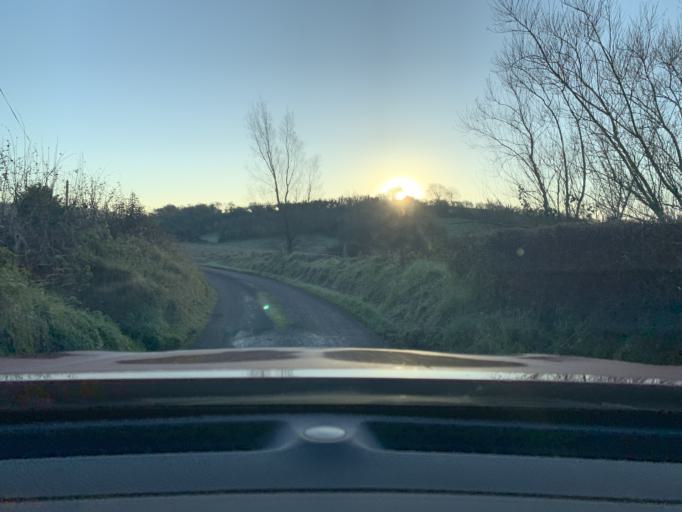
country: IE
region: Connaught
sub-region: Sligo
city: Ballymote
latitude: 54.0619
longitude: -8.5263
